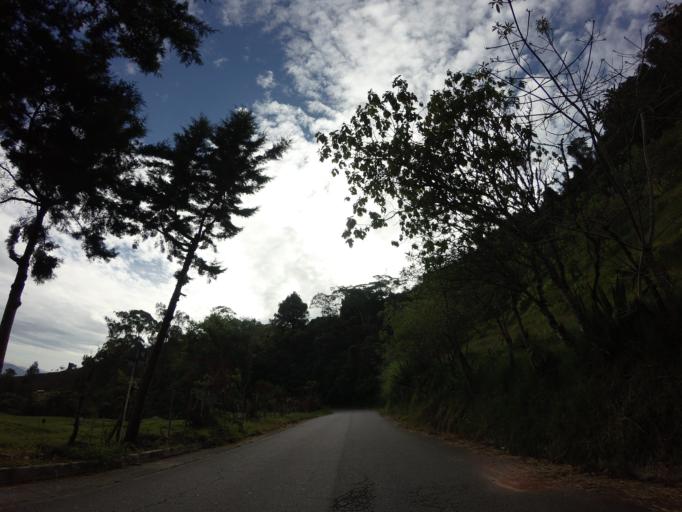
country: CO
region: Tolima
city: Casabianca
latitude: 5.1391
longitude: -75.1296
